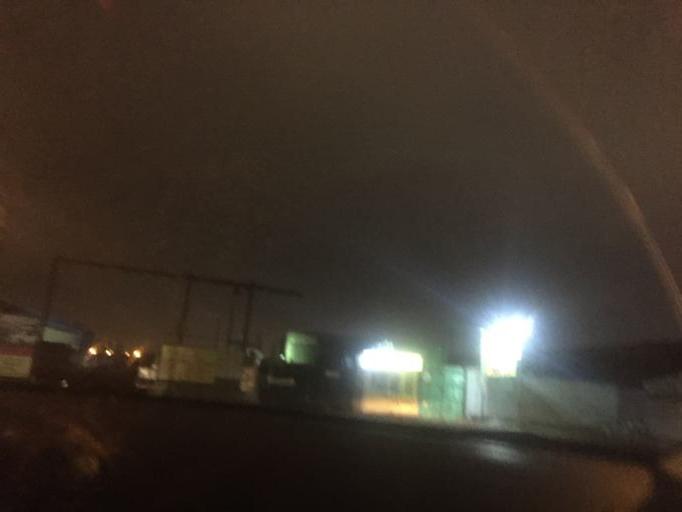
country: KZ
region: Astana Qalasy
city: Astana
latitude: 51.1825
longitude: 71.3858
